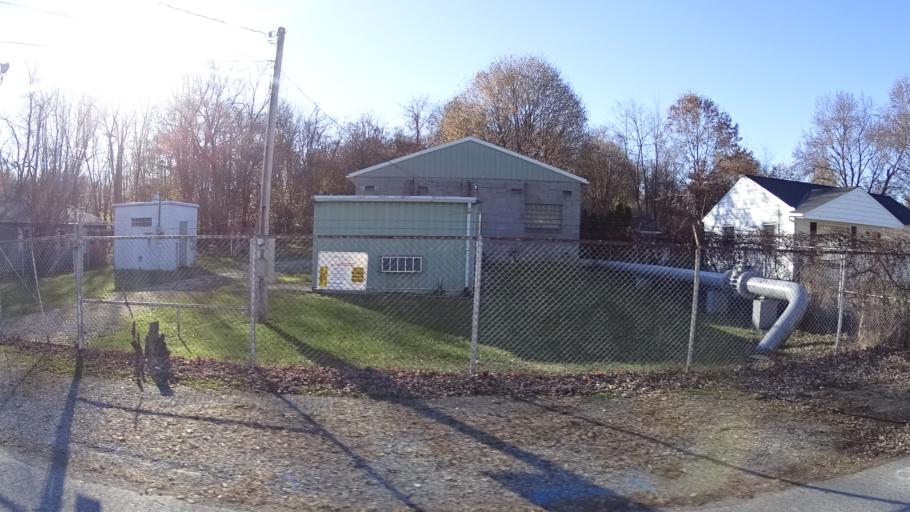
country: US
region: Ohio
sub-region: Lorain County
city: Sheffield
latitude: 41.4179
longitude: -82.1087
